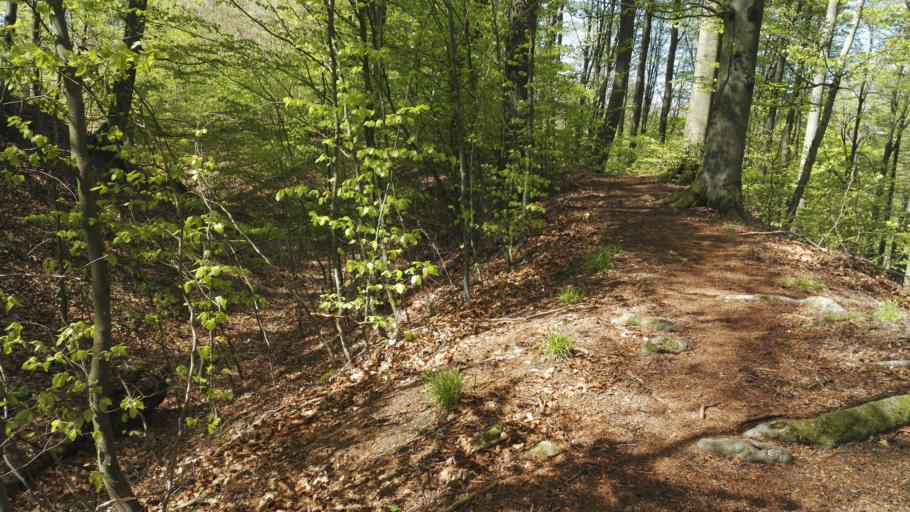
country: DE
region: North Rhine-Westphalia
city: Lichtenau
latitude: 51.5385
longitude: 8.9352
